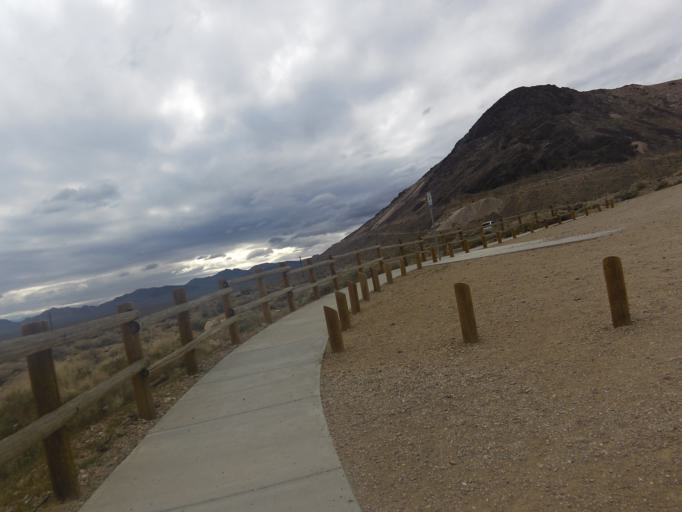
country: US
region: Nevada
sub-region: Nye County
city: Beatty
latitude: 36.8973
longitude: -116.8292
